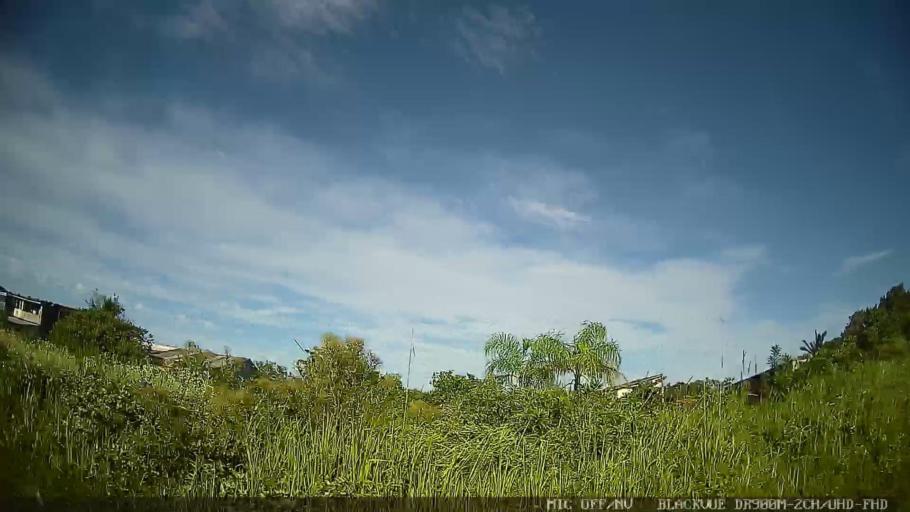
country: BR
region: Sao Paulo
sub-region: Iguape
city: Iguape
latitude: -24.7605
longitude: -47.5753
